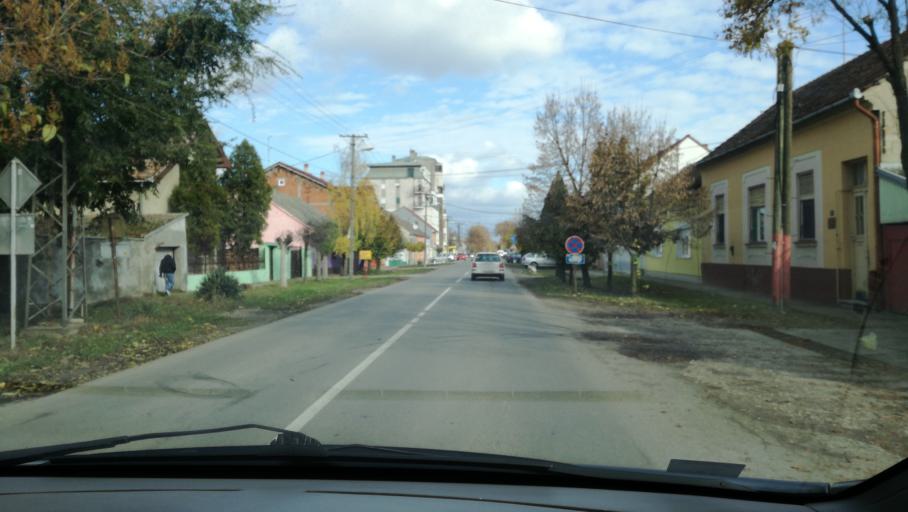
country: RS
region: Autonomna Pokrajina Vojvodina
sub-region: Severnobanatski Okrug
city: Kikinda
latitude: 45.8261
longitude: 20.4658
